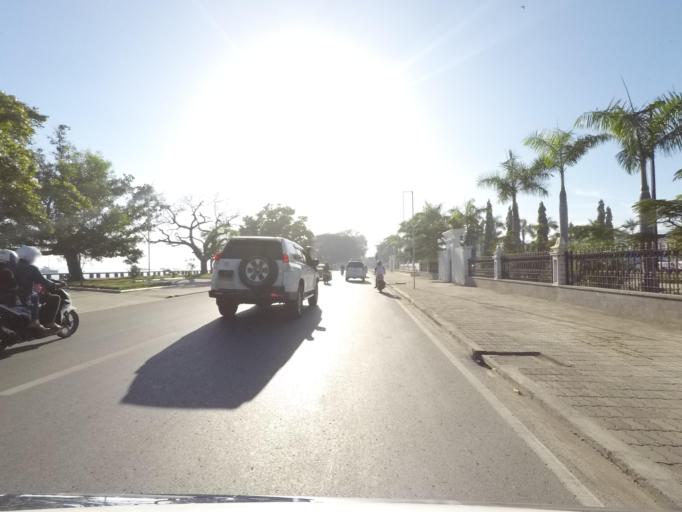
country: TL
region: Dili
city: Dili
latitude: -8.5535
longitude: 125.5775
